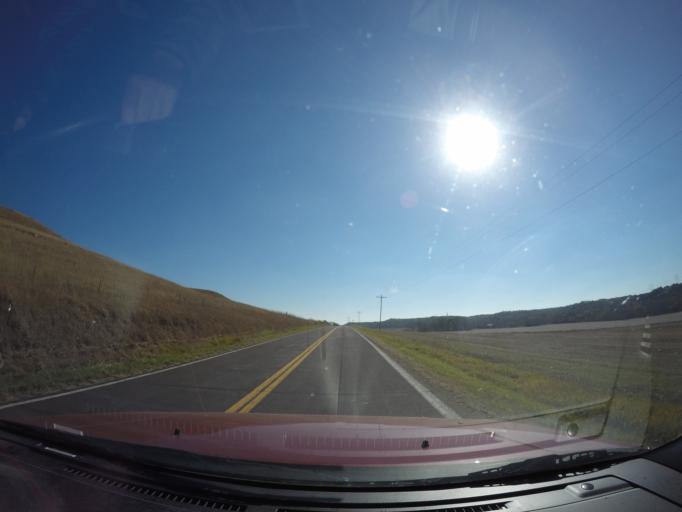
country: US
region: Kansas
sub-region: Geary County
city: Grandview Plaza
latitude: 38.9884
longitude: -96.7261
